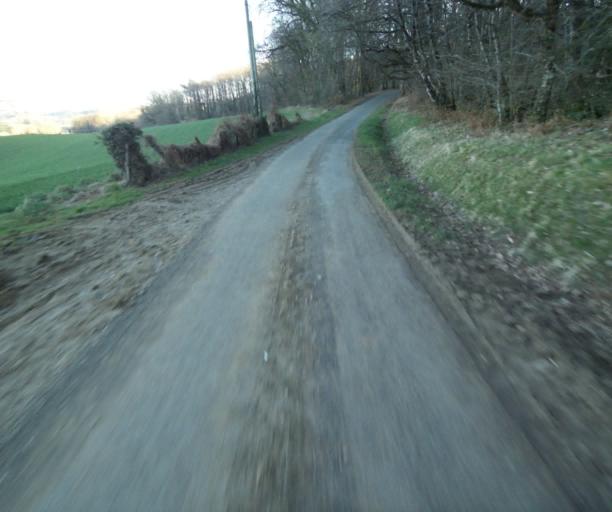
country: FR
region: Limousin
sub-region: Departement de la Correze
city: Seilhac
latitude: 45.3500
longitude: 1.7207
